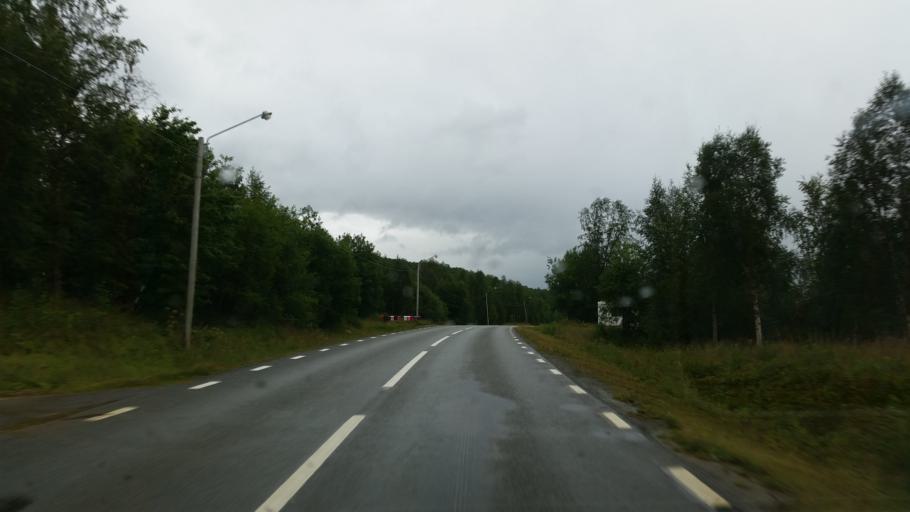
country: NO
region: Nordland
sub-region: Rana
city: Mo i Rana
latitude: 65.8658
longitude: 15.0189
